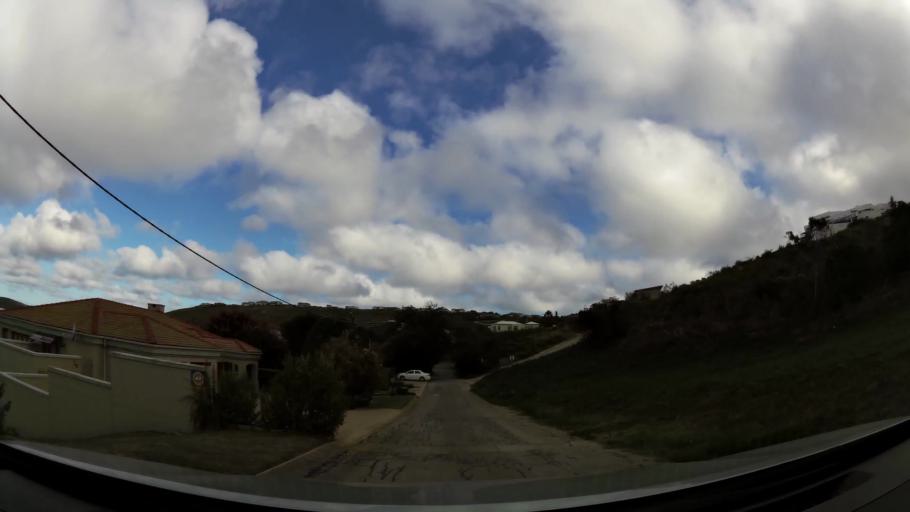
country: ZA
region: Western Cape
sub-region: Eden District Municipality
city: Plettenberg Bay
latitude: -34.0829
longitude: 23.3608
